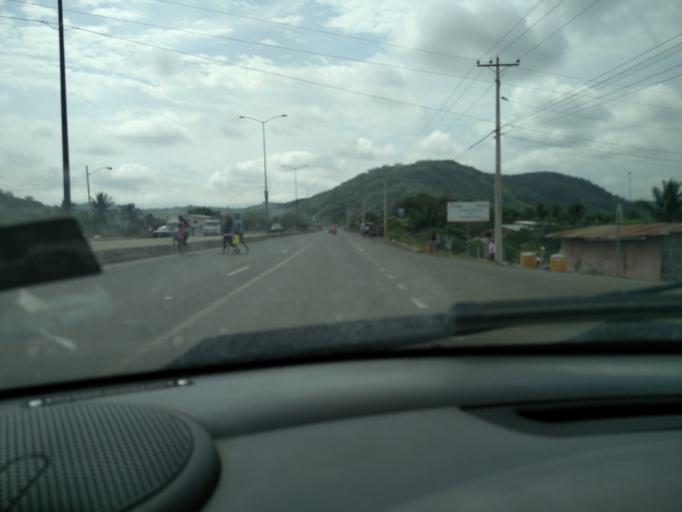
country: EC
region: Manabi
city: Portoviejo
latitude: -0.9894
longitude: -80.4699
